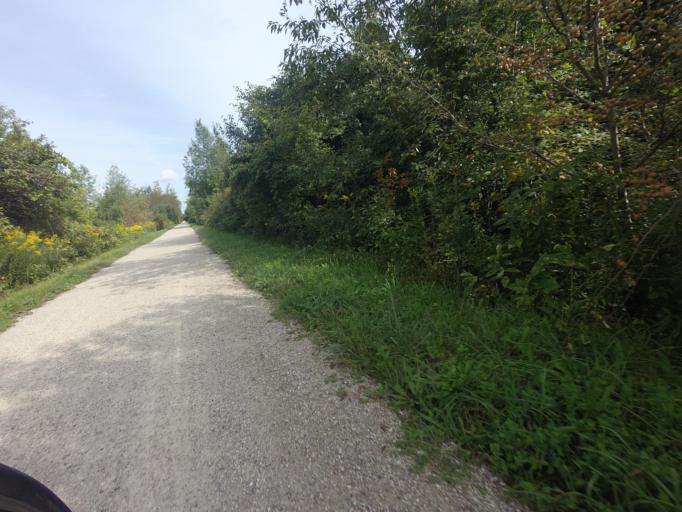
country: CA
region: Ontario
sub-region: Wellington County
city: Guelph
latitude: 43.5740
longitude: -80.3583
